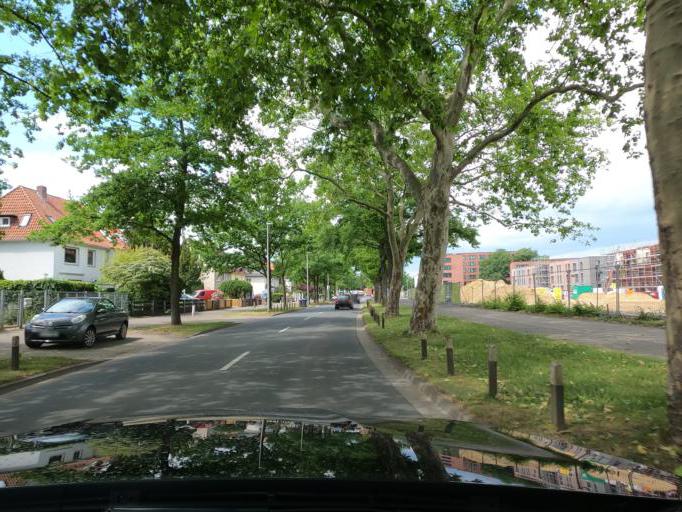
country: DE
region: Lower Saxony
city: Isernhagen Farster Bauerschaft
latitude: 52.4060
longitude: 9.8078
